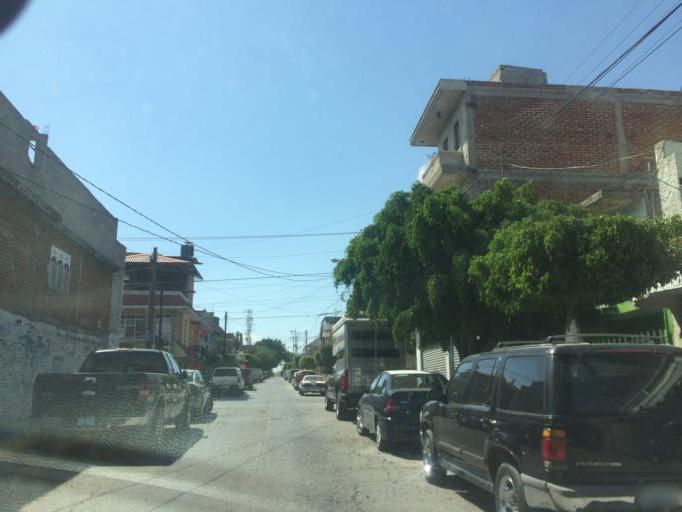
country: MX
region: Guanajuato
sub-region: Leon
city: La Ermita
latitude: 21.1355
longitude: -101.7064
